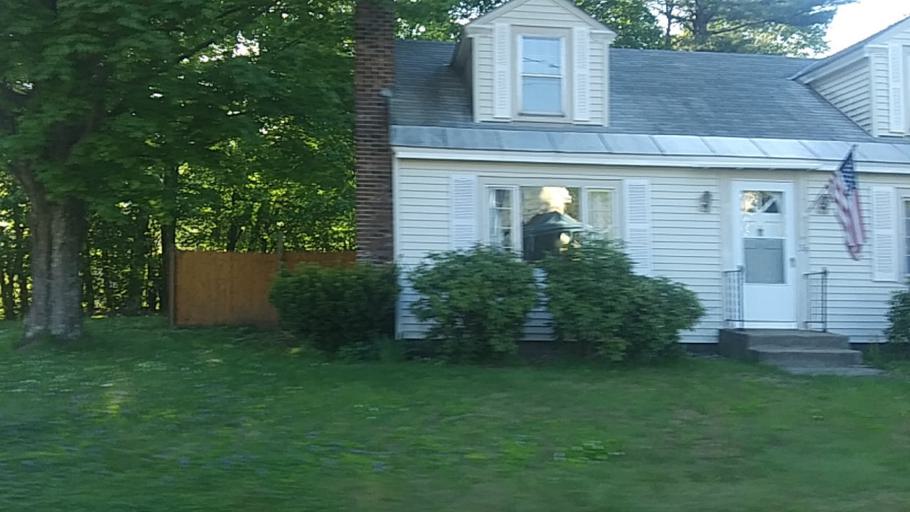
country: US
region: Massachusetts
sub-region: Franklin County
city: Shelburne Falls
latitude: 42.5997
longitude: -72.7404
